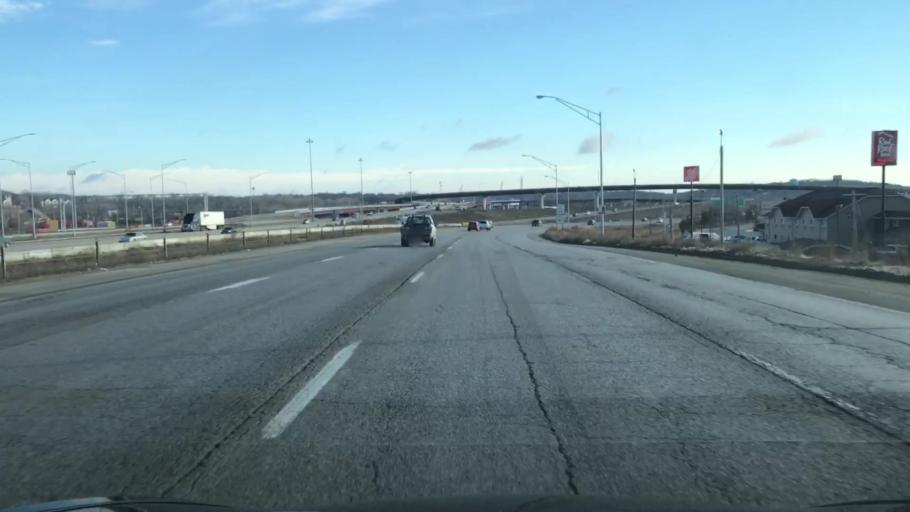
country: US
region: Iowa
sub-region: Pottawattamie County
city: Council Bluffs
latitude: 41.2320
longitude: -95.8490
